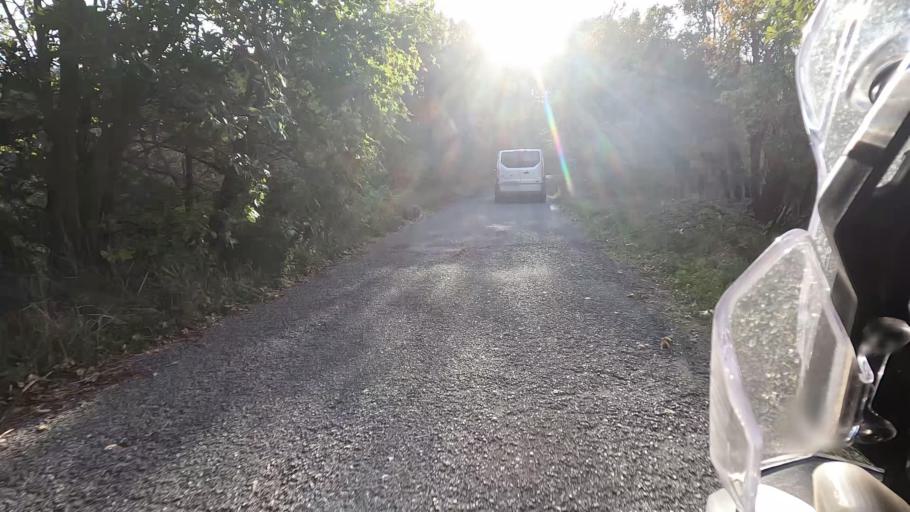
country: IT
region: Liguria
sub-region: Provincia di Savona
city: Urbe
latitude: 44.4530
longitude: 8.5817
